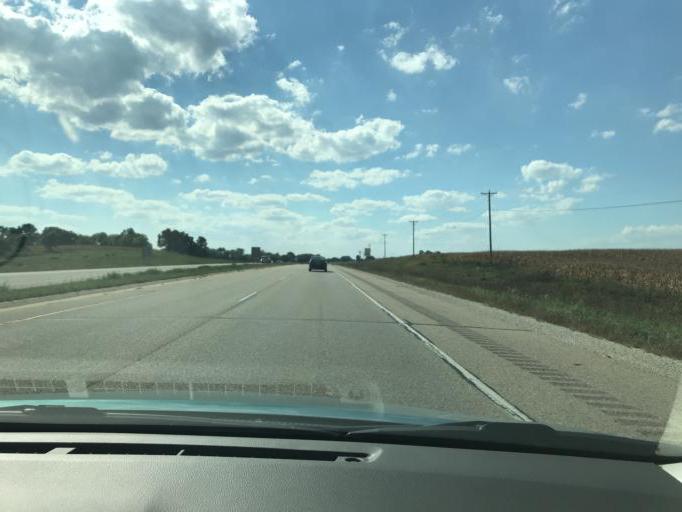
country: US
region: Wisconsin
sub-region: Kenosha County
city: Powers Lake
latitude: 42.5831
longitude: -88.2977
